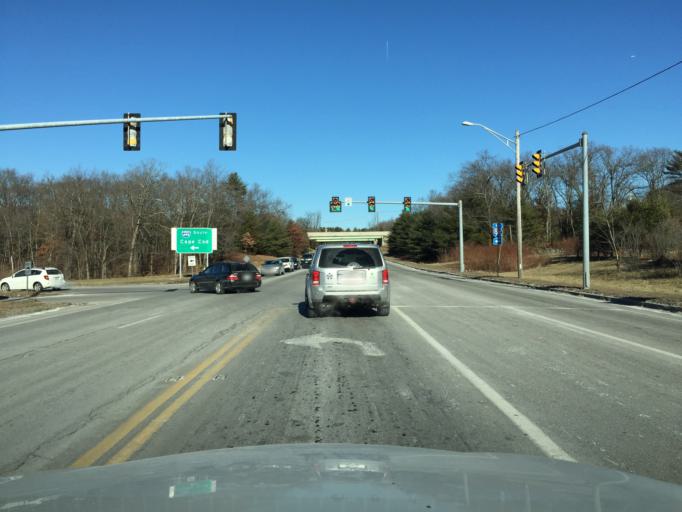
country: US
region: Massachusetts
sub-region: Norfolk County
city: Wrentham
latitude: 42.0382
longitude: -71.3462
